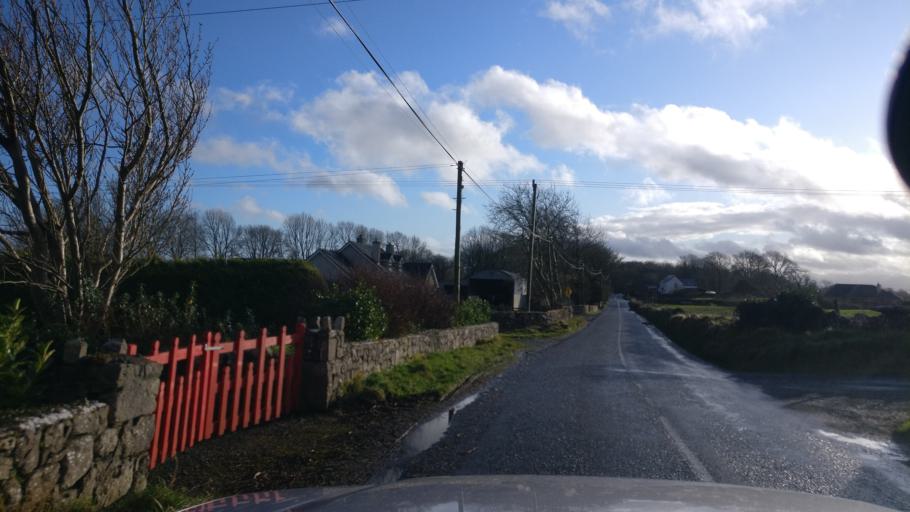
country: IE
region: Connaught
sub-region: County Galway
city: Loughrea
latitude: 53.2606
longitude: -8.6263
